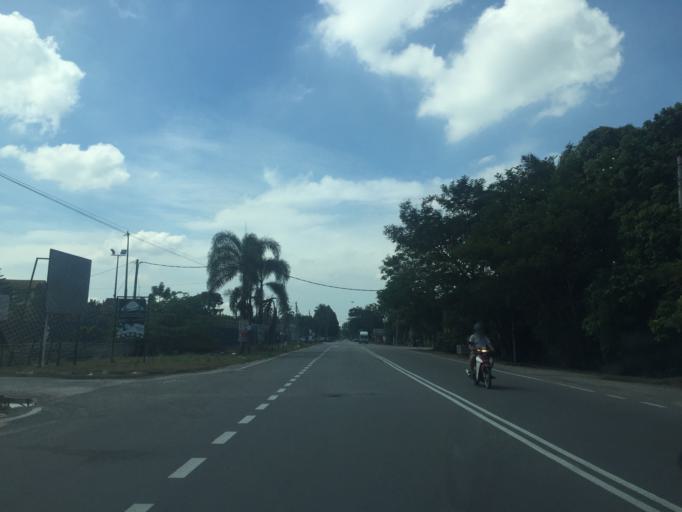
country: MY
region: Penang
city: Tasek Glugor
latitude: 5.5029
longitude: 100.5242
